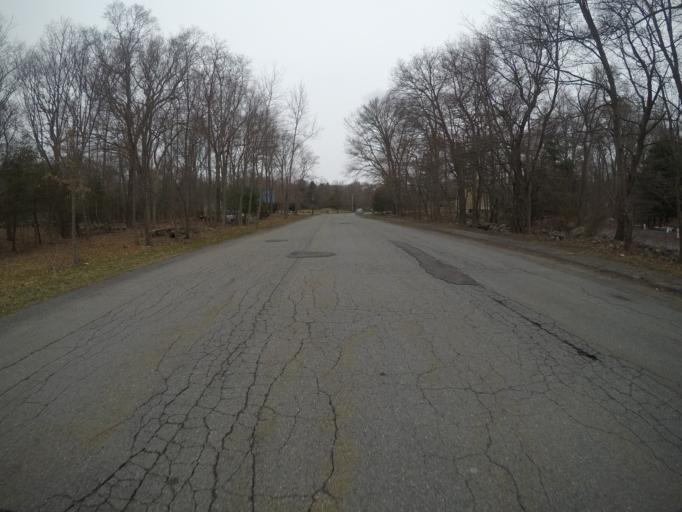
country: US
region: Massachusetts
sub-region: Bristol County
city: Easton
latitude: 42.0516
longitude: -71.1450
